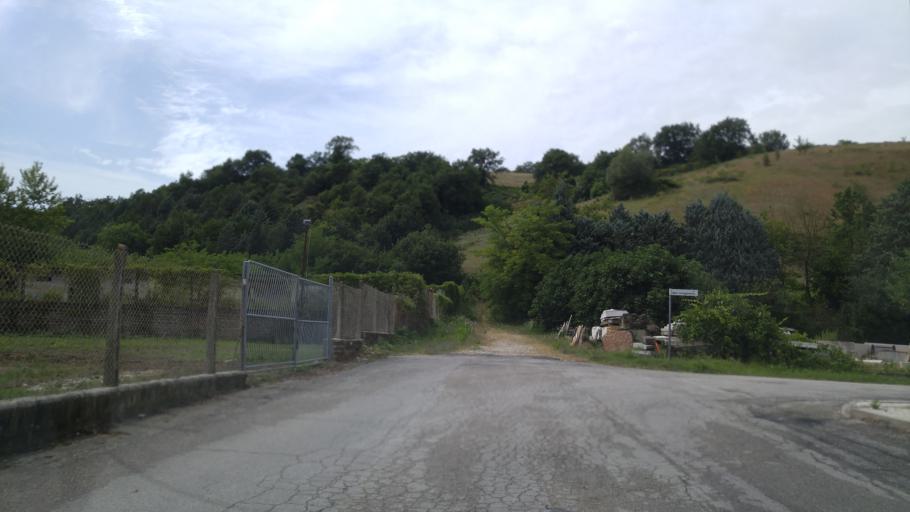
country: IT
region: The Marches
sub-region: Provincia di Pesaro e Urbino
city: Acqualagna
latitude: 43.6309
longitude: 12.6827
